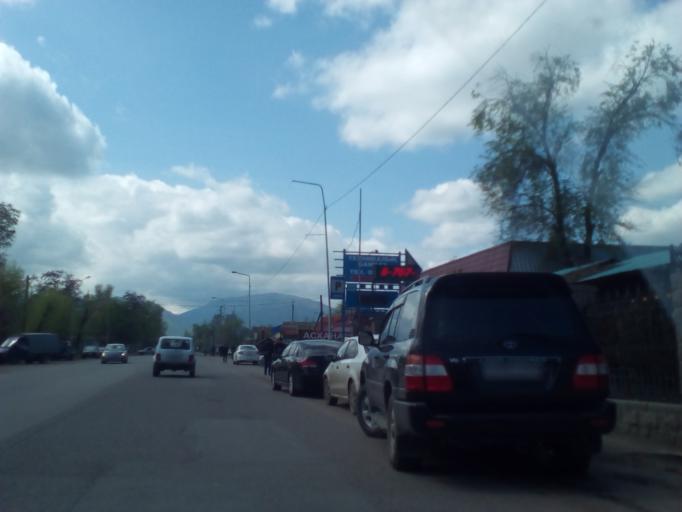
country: KZ
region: Almaty Oblysy
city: Burunday
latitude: 43.2118
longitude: 76.6420
